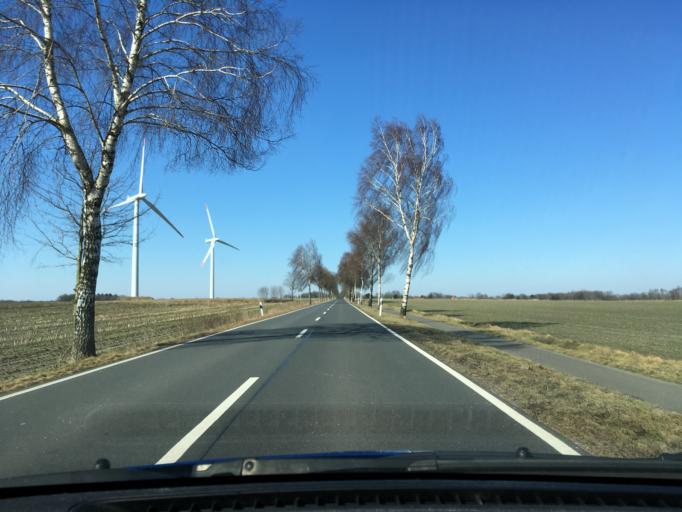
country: DE
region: Lower Saxony
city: Hemslingen
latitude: 53.0722
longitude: 9.6351
